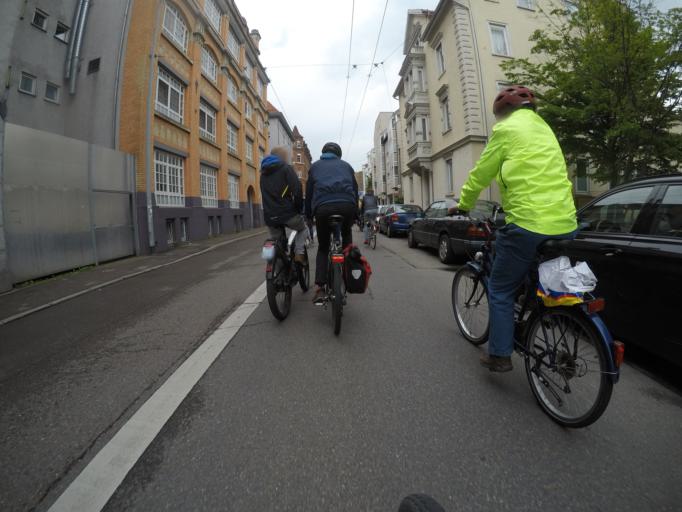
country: DE
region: Baden-Wuerttemberg
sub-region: Regierungsbezirk Stuttgart
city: Esslingen
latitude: 48.7419
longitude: 9.3009
